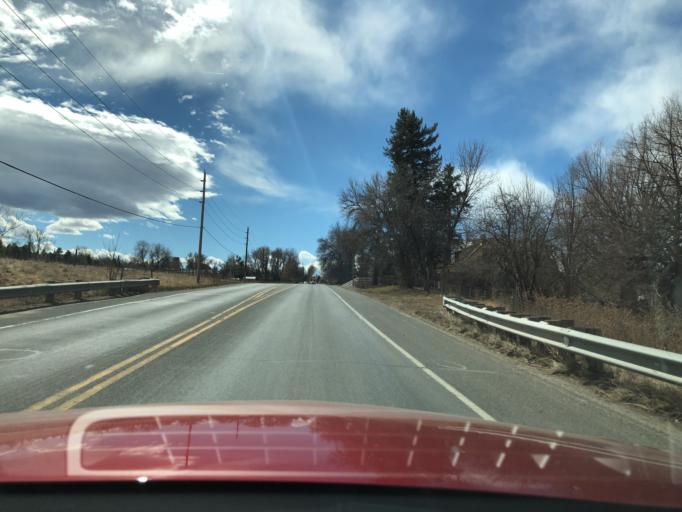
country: US
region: Colorado
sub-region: Boulder County
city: Gunbarrel
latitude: 40.0091
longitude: -105.1783
